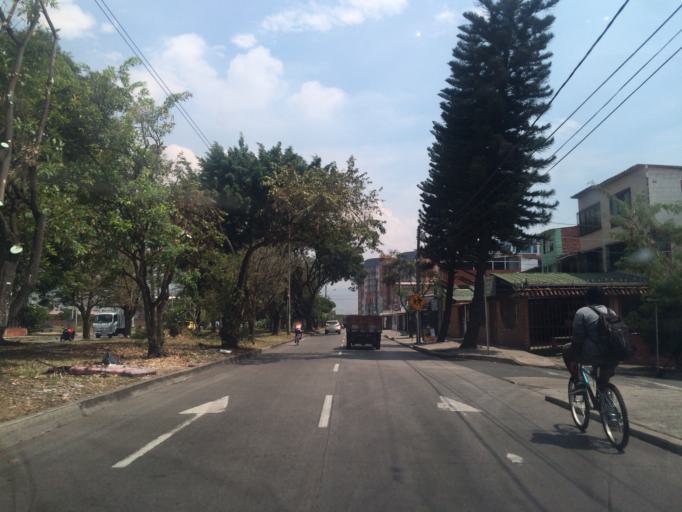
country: CO
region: Valle del Cauca
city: Cali
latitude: 3.4734
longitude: -76.5033
